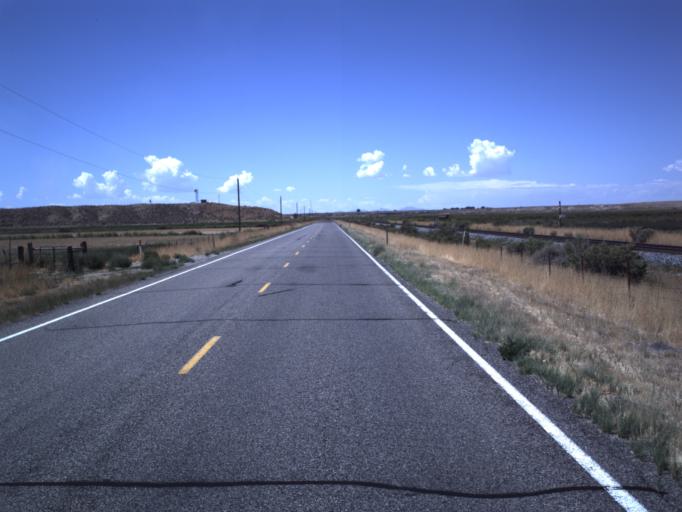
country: US
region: Utah
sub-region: Millard County
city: Delta
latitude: 39.5338
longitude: -112.3013
